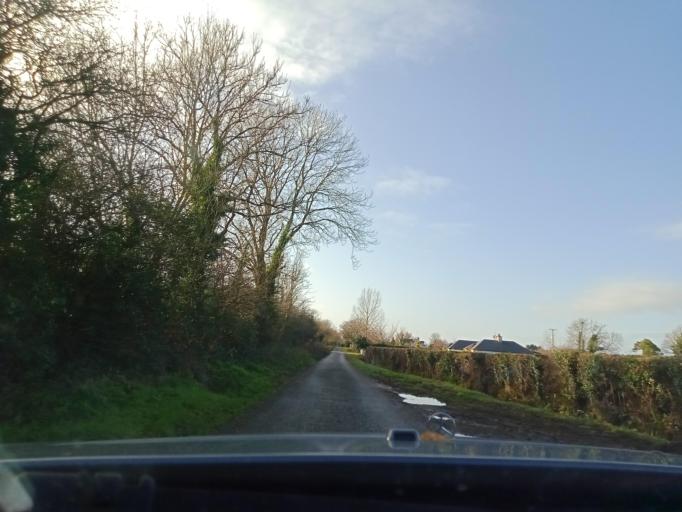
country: IE
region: Leinster
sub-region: Kilkenny
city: Callan
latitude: 52.5241
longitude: -7.3932
